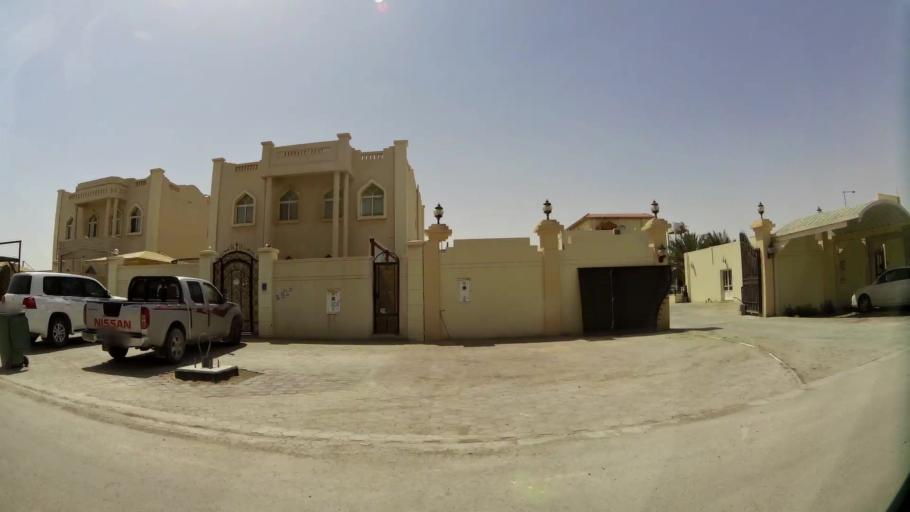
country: QA
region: Baladiyat Umm Salal
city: Umm Salal Muhammad
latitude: 25.3775
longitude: 51.4466
